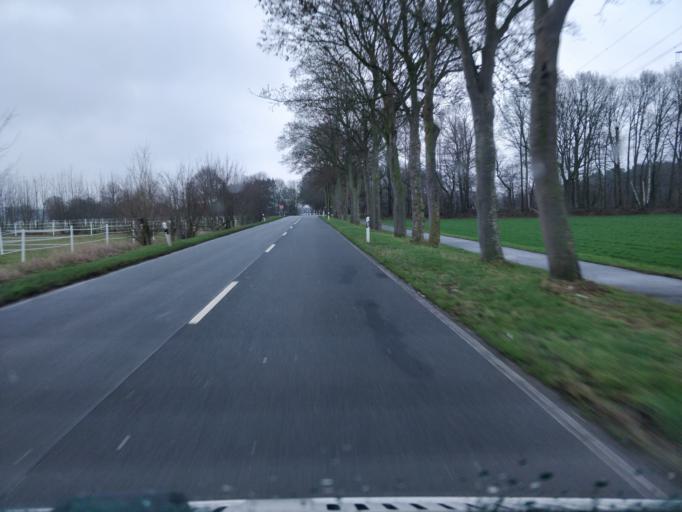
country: DE
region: North Rhine-Westphalia
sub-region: Regierungsbezirk Dusseldorf
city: Mehrhoog
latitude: 51.7455
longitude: 6.5431
